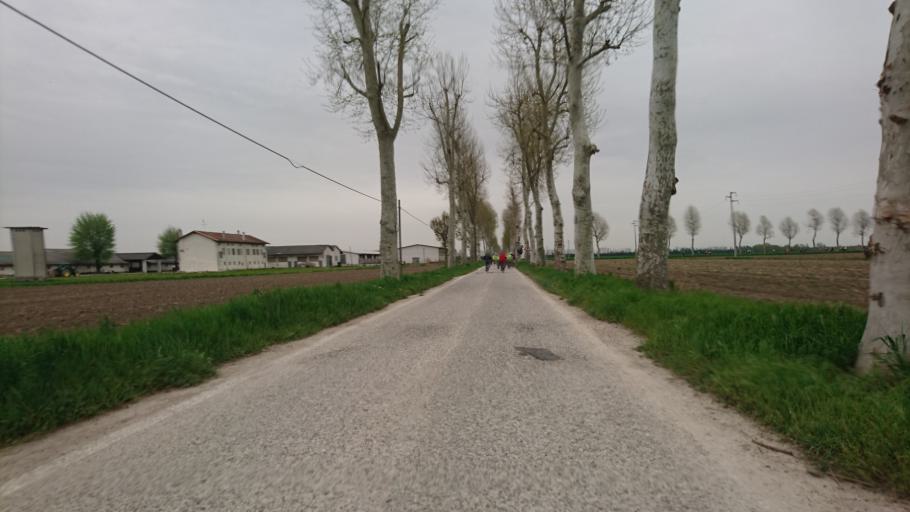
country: IT
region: Veneto
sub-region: Provincia di Venezia
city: Lugugnana
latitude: 45.6927
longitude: 12.9753
